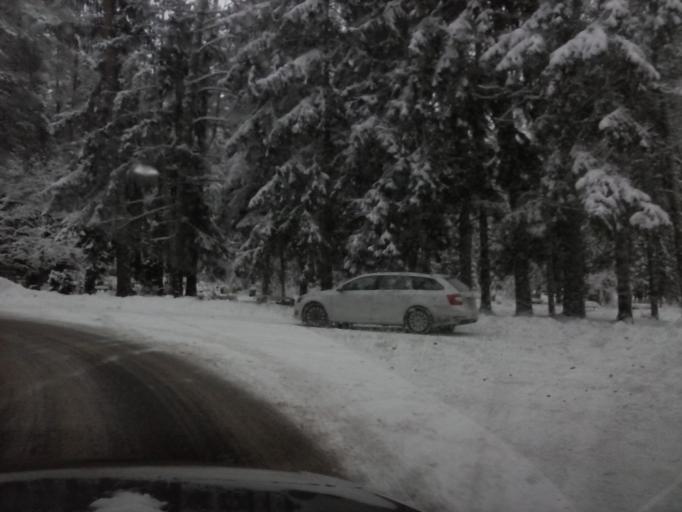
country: EE
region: Tartu
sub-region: Elva linn
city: Elva
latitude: 58.2118
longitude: 26.4219
